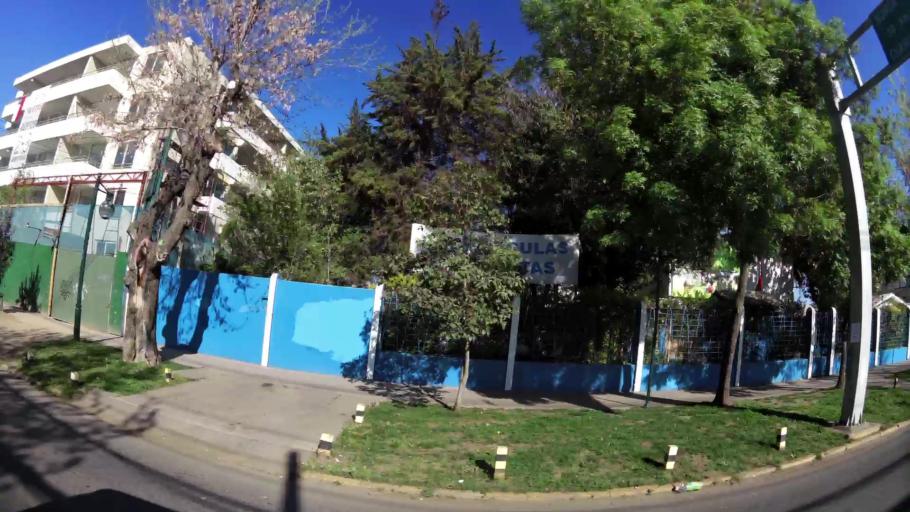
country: CL
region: Santiago Metropolitan
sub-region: Provincia de Santiago
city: Villa Presidente Frei, Nunoa, Santiago, Chile
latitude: -33.4523
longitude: -70.5804
